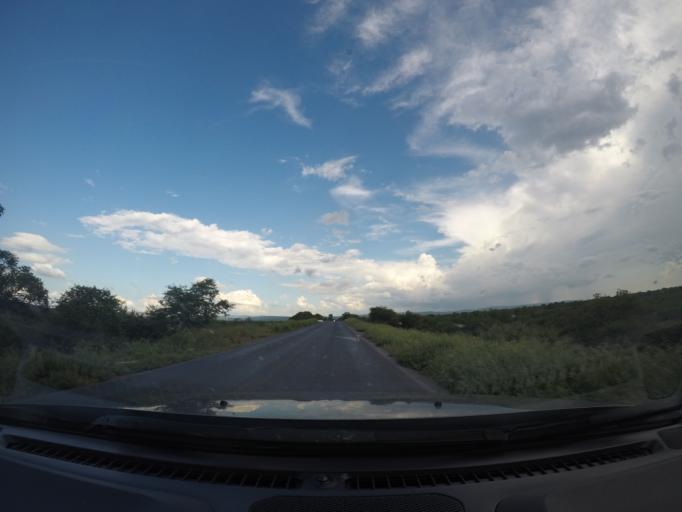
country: BR
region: Bahia
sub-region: Ibotirama
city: Ibotirama
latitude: -12.1613
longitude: -43.2896
